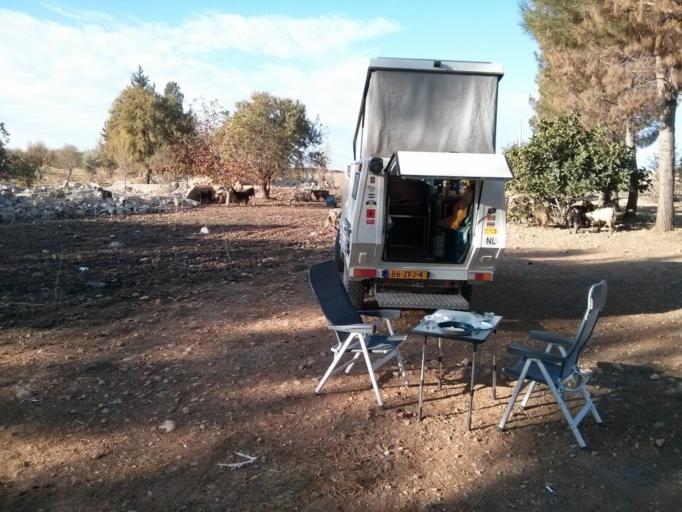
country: TR
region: Sanliurfa
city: Bozova
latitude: 37.3473
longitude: 38.5147
